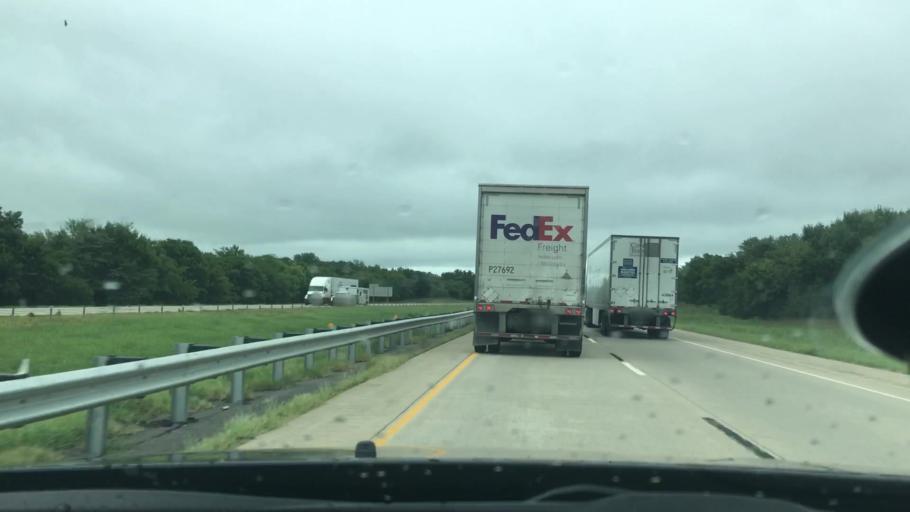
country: US
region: Oklahoma
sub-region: McIntosh County
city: Checotah
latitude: 35.4590
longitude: -95.6255
